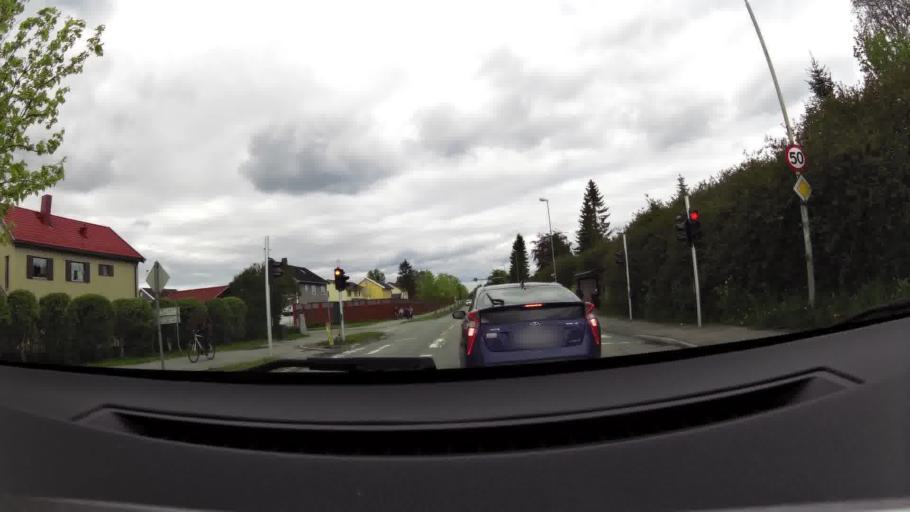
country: NO
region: Sor-Trondelag
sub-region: Trondheim
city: Trondheim
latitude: 63.4046
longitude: 10.4273
